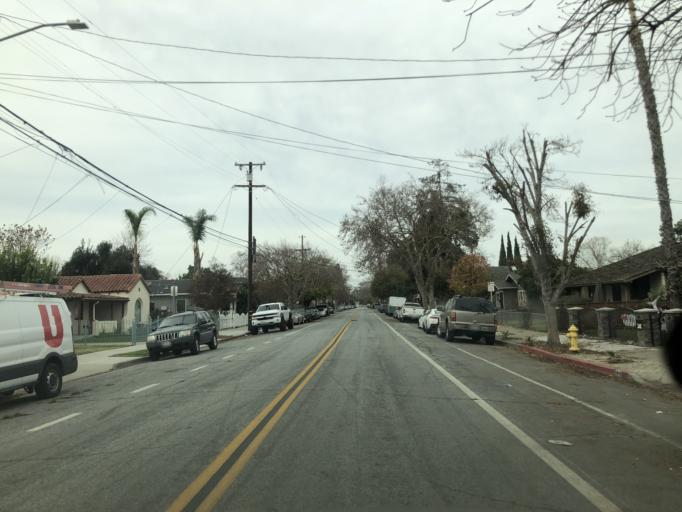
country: US
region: California
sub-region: Santa Clara County
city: San Jose
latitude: 37.3412
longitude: -121.8663
